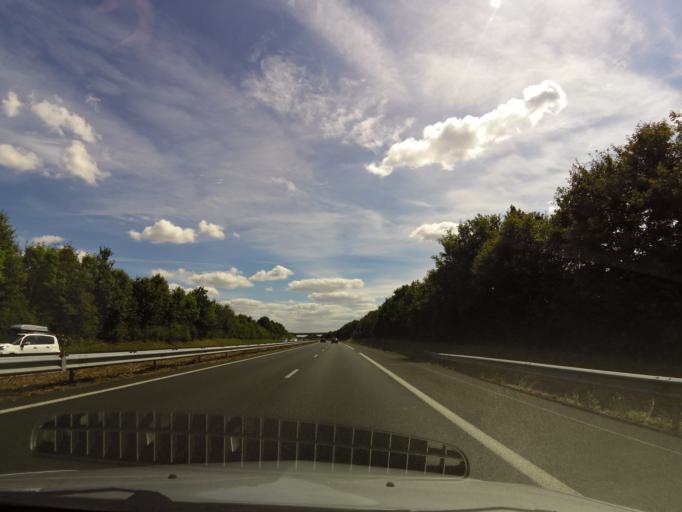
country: FR
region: Pays de la Loire
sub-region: Departement de la Vendee
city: Chauche
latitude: 46.8637
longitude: -1.2837
